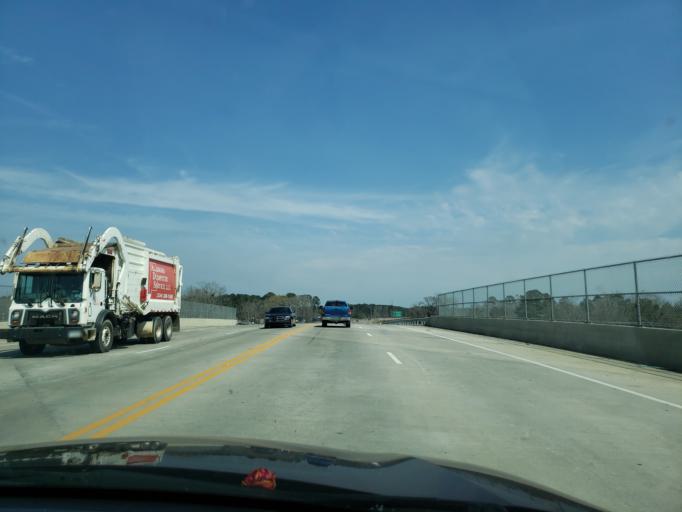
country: US
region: Alabama
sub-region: Elmore County
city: Elmore
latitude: 32.5385
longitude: -86.3151
